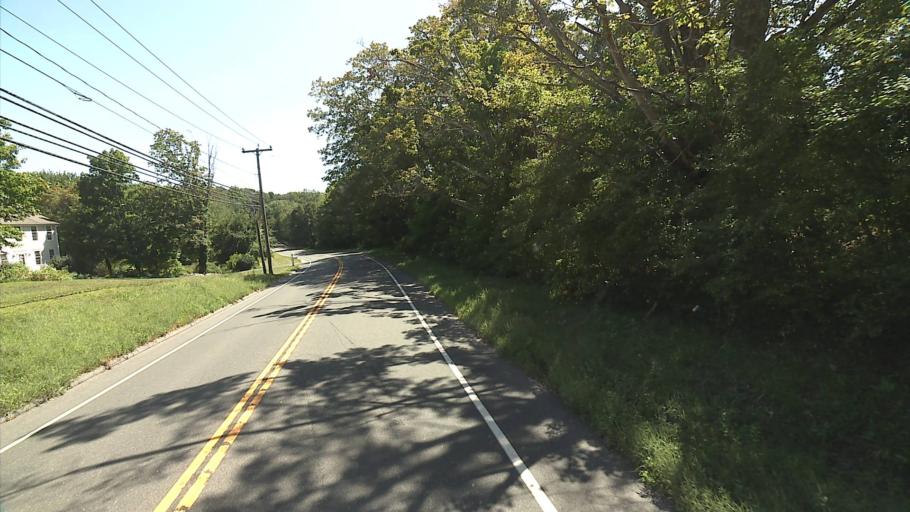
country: US
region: Connecticut
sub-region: New Haven County
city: Oxford
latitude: 41.4097
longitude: -73.1453
